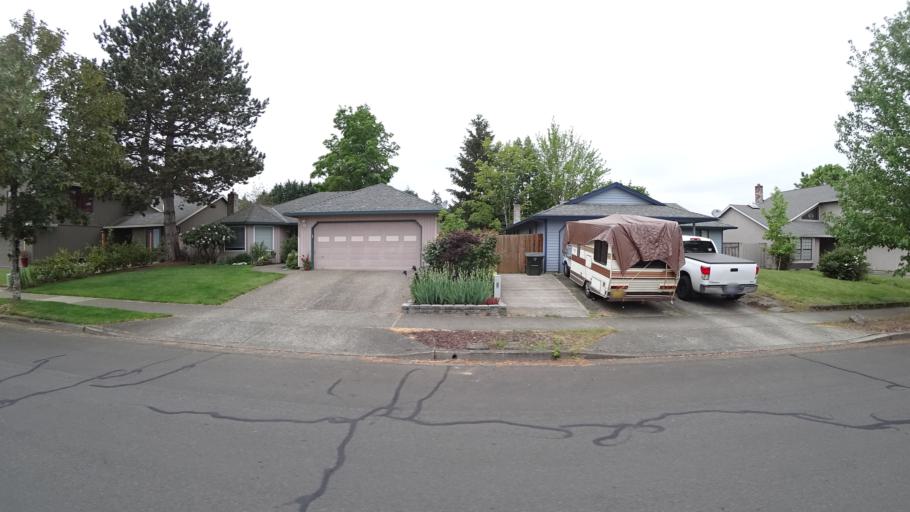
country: US
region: Oregon
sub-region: Washington County
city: Aloha
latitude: 45.5044
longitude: -122.9056
